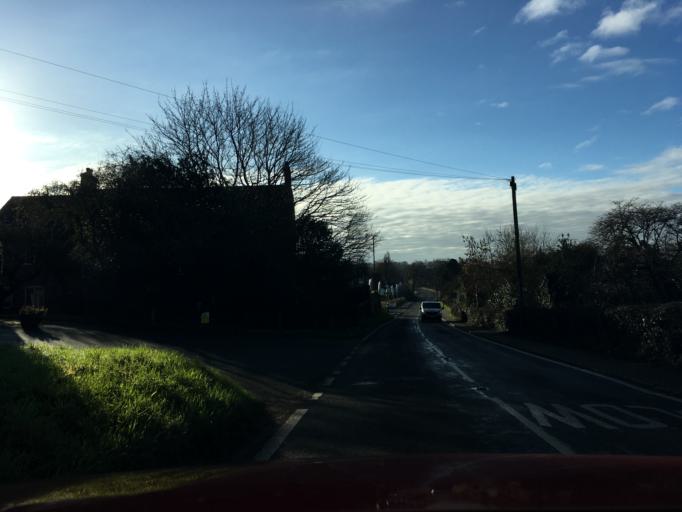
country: GB
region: England
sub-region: Staffordshire
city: Burton upon Trent
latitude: 52.8174
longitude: -1.6081
